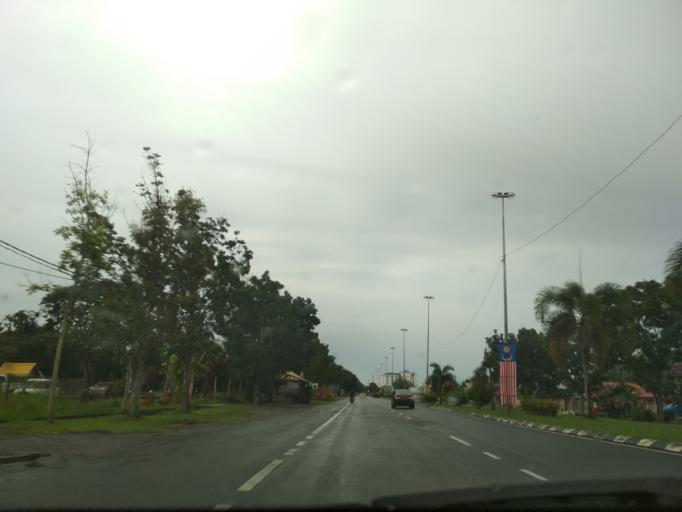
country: MY
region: Perlis
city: Kangar
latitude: 6.4232
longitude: 100.1842
